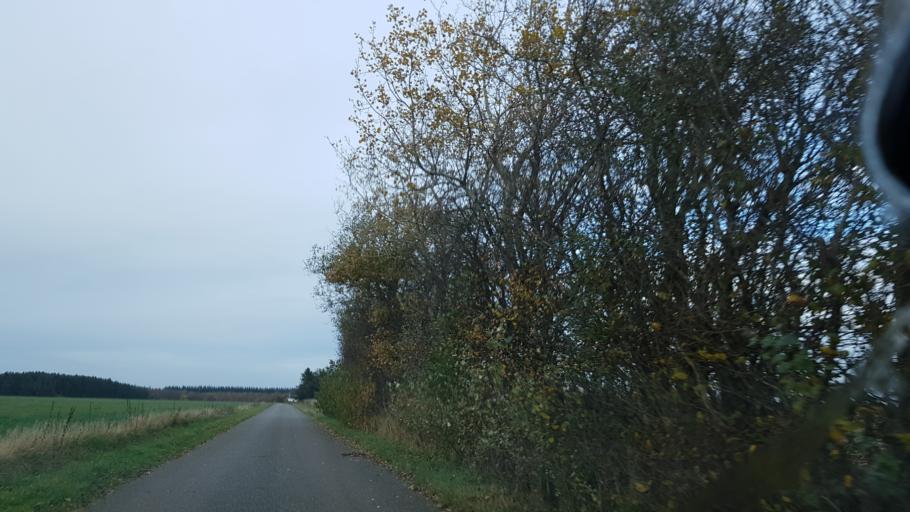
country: DK
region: South Denmark
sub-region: Haderslev Kommune
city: Vojens
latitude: 55.2888
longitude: 9.2063
